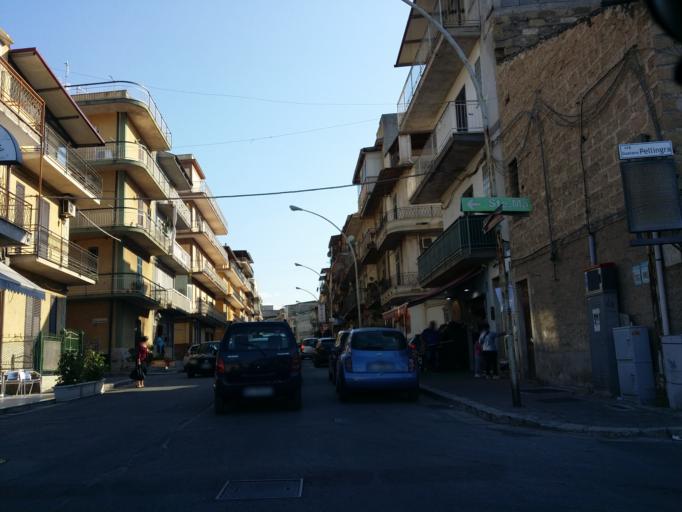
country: IT
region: Sicily
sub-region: Palermo
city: Misilmeri
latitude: 38.0290
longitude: 13.4494
